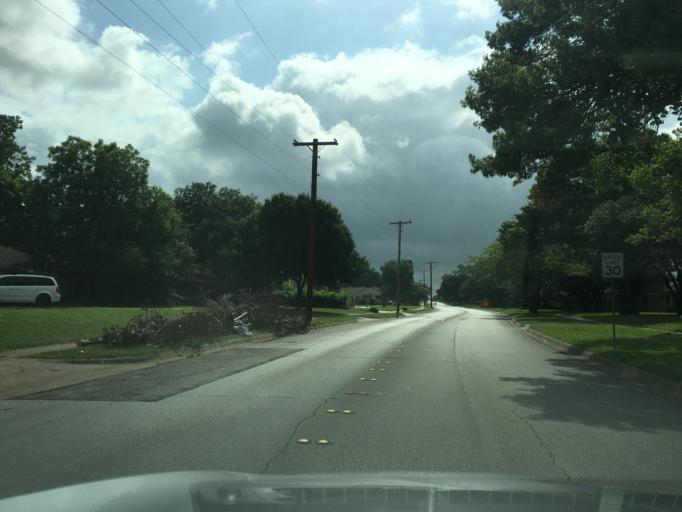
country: US
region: Texas
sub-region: Dallas County
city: Richardson
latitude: 32.9400
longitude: -96.7266
